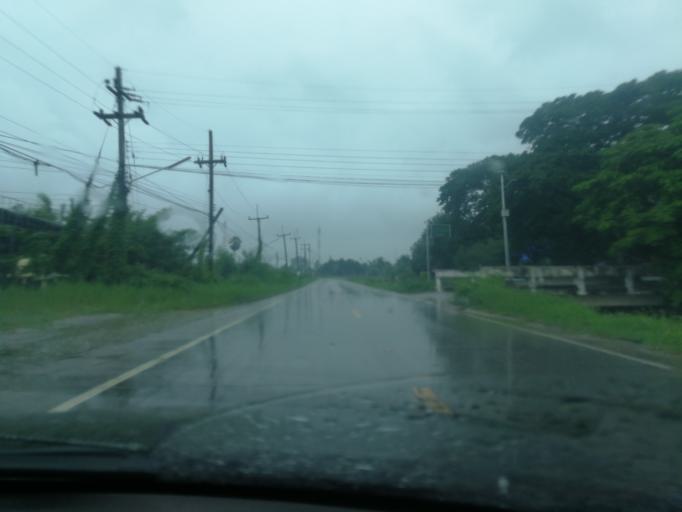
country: TH
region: Chiang Mai
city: San Pa Tong
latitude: 18.6258
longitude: 98.8987
